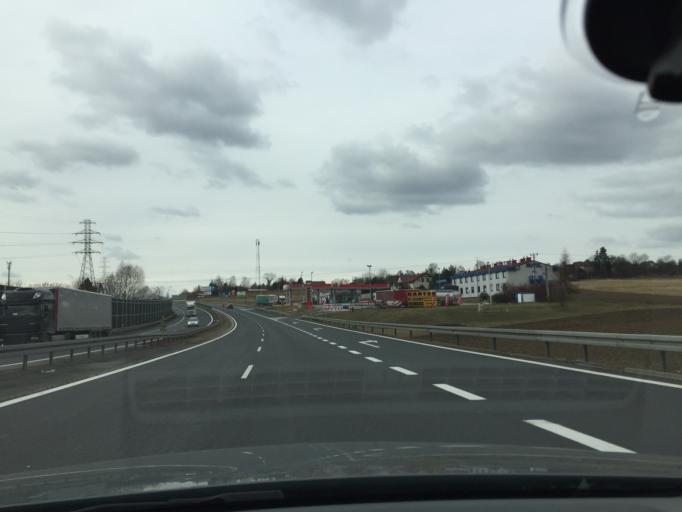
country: PL
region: Silesian Voivodeship
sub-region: Powiat cieszynski
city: Zamarski
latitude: 49.7658
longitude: 18.6557
